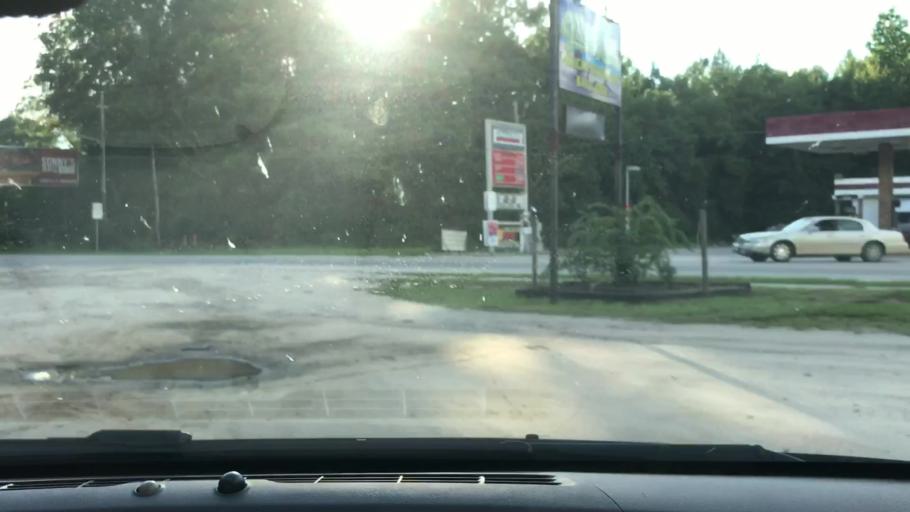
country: US
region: Florida
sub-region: Jackson County
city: Graceville
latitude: 30.9662
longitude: -85.5131
